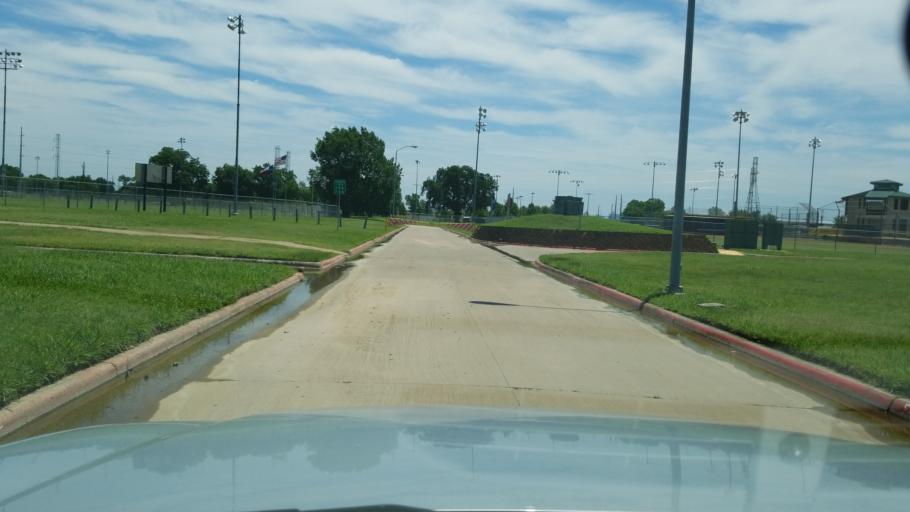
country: US
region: Texas
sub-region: Dallas County
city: Irving
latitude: 32.8118
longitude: -96.9131
